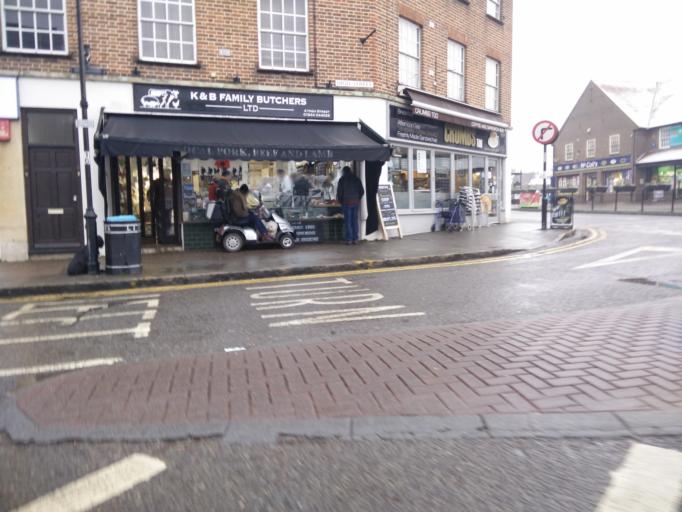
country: GB
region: England
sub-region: Buckinghamshire
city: Princes Risborough
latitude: 51.7231
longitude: -0.8304
